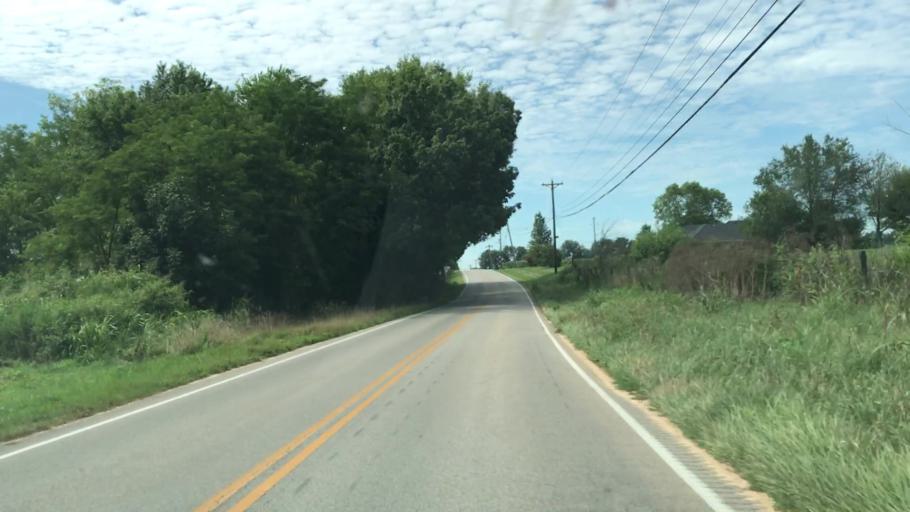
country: US
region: Kentucky
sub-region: Edmonson County
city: Brownsville
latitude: 37.0631
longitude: -86.2114
